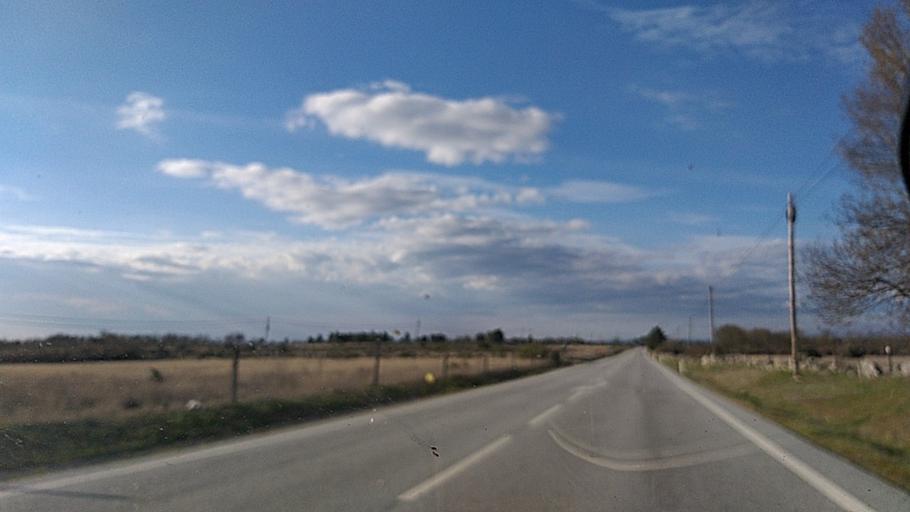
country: ES
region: Castille and Leon
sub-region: Provincia de Salamanca
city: Fuentes de Onoro
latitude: 40.6268
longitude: -6.8496
